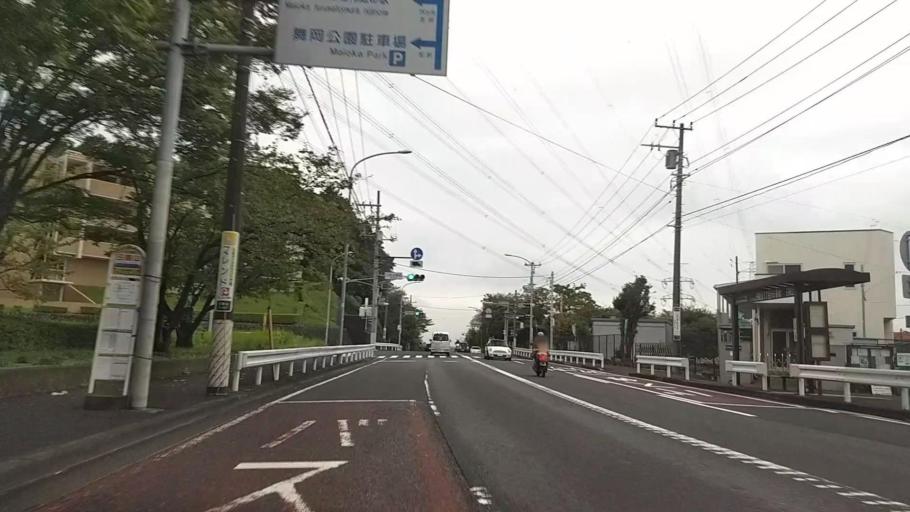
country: JP
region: Kanagawa
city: Kamakura
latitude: 35.3983
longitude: 139.5609
